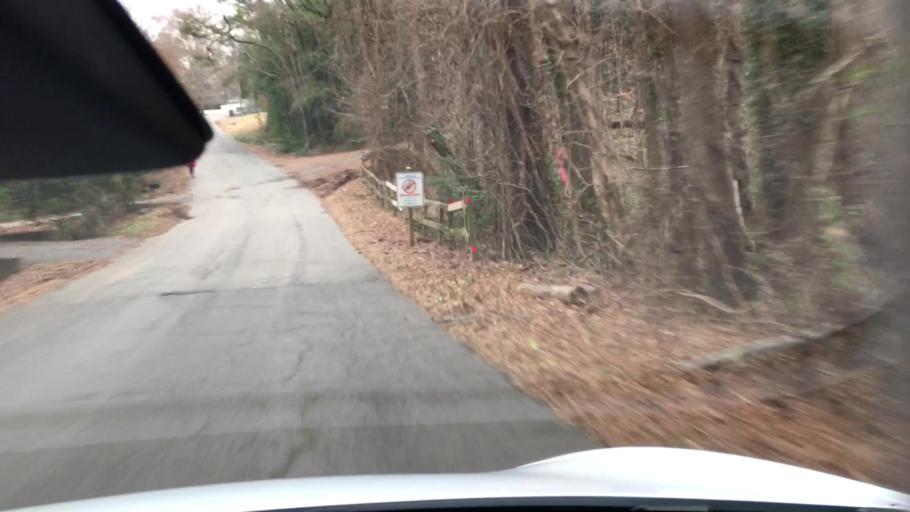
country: US
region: Virginia
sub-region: Chesterfield County
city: Bon Air
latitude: 37.5301
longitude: -77.5707
